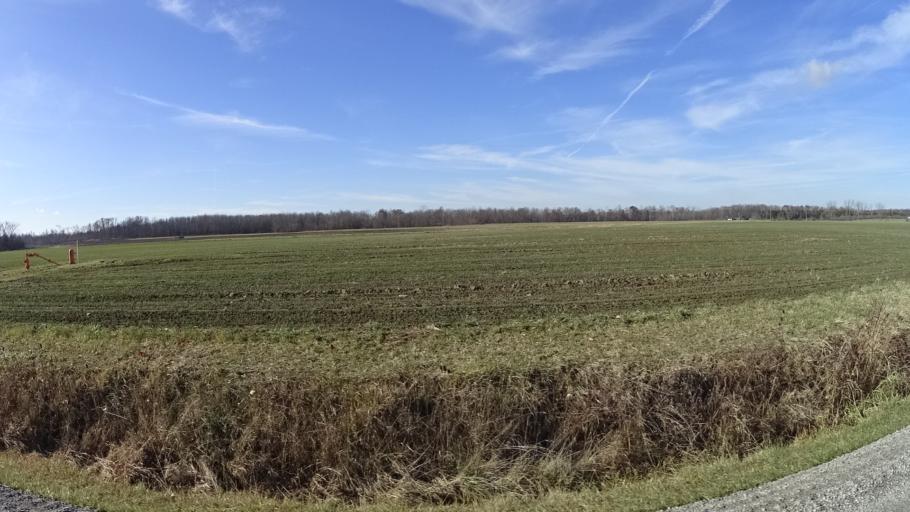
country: US
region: Ohio
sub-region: Lorain County
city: Wellington
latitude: 41.1127
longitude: -82.2004
